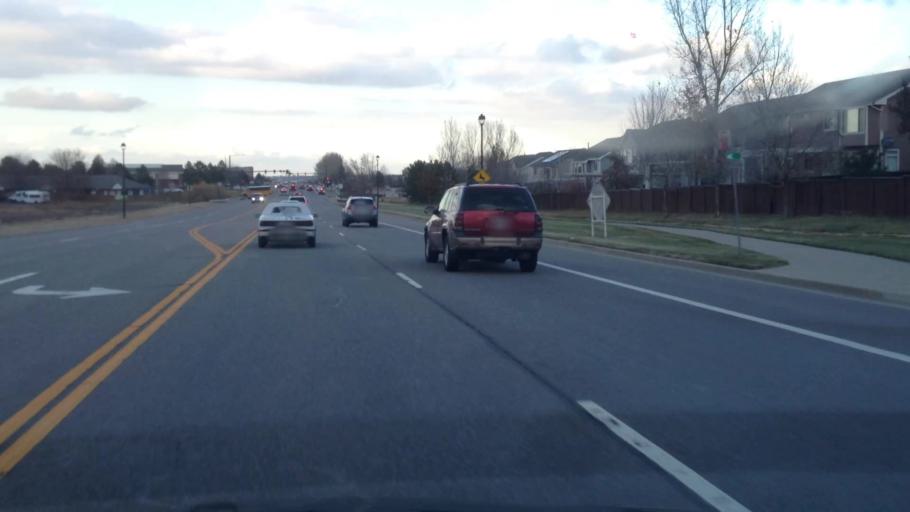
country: US
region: Colorado
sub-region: Douglas County
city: Stonegate
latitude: 39.5302
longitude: -104.7934
